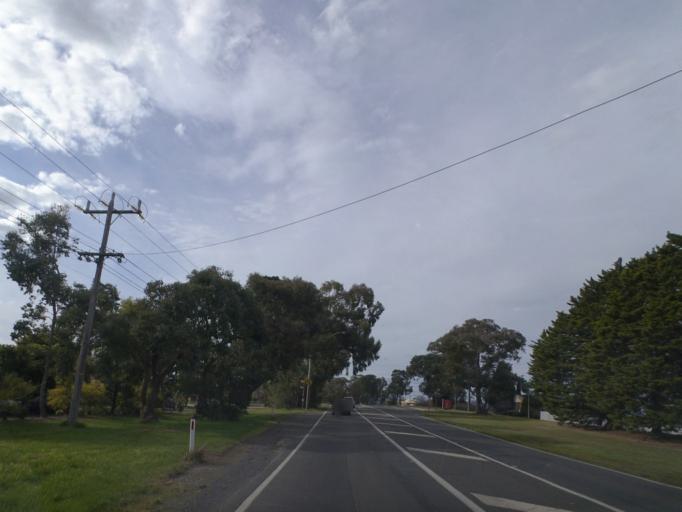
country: AU
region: Victoria
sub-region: Manningham
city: Donvale
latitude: -37.7736
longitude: 145.1691
